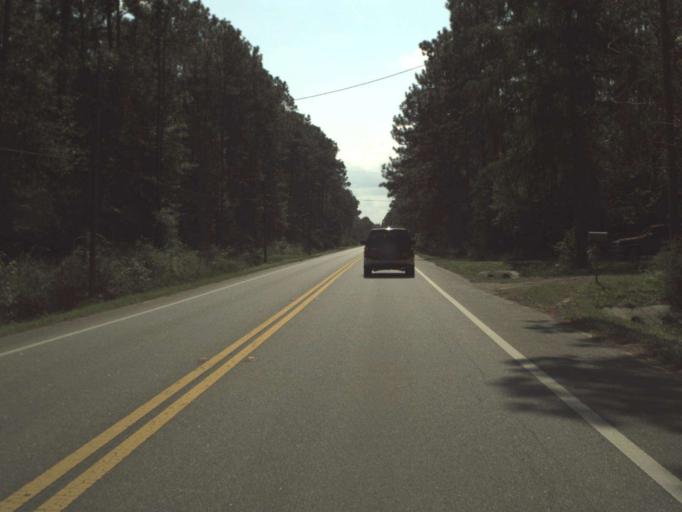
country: US
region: Florida
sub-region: Holmes County
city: Bonifay
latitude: 30.8151
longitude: -85.6725
